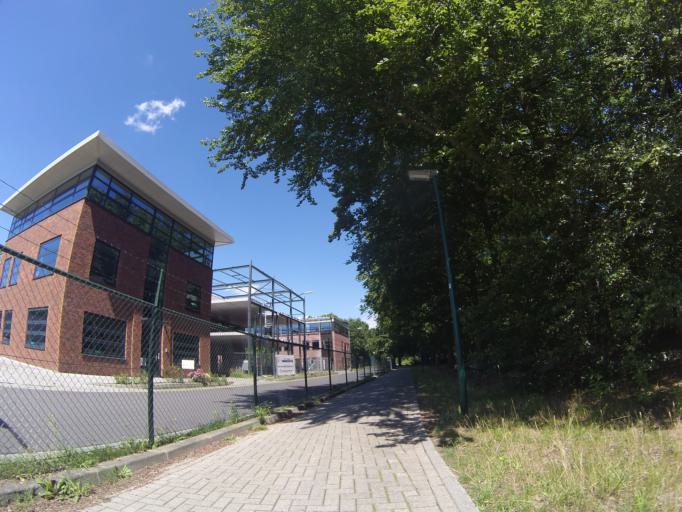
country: NL
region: Utrecht
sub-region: Gemeente De Bilt
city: De Bilt
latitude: 52.1208
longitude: 5.1790
